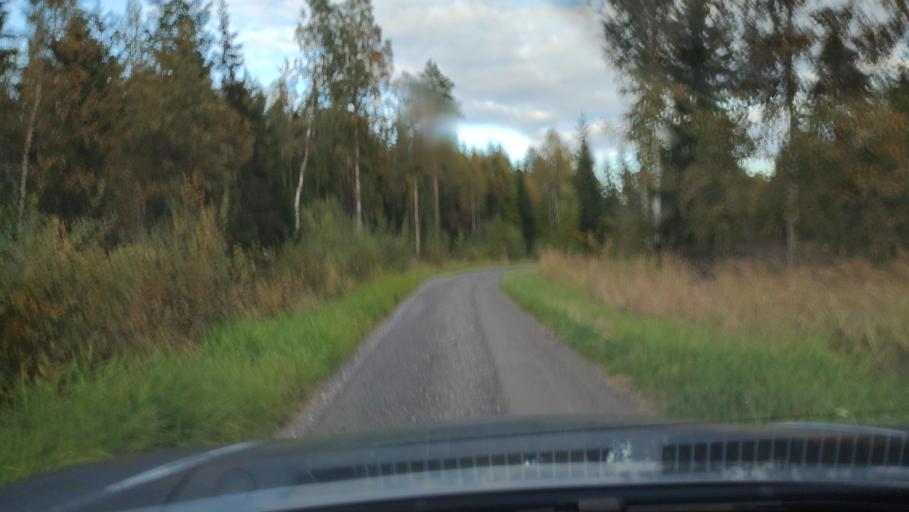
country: FI
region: Ostrobothnia
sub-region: Sydosterbotten
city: Kristinestad
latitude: 62.2323
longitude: 21.4048
